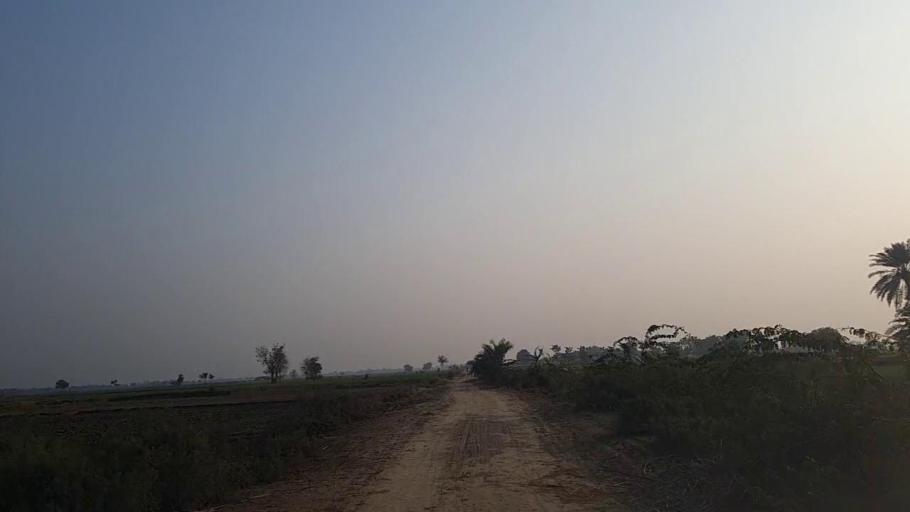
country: PK
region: Sindh
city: Nawabshah
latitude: 26.2339
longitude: 68.4678
